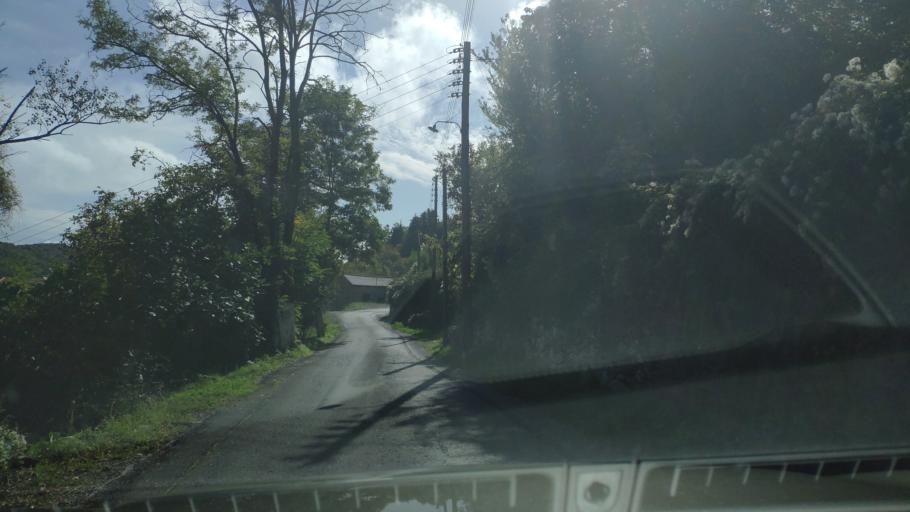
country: GR
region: Peloponnese
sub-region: Nomos Arkadias
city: Dimitsana
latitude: 37.5891
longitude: 22.0212
